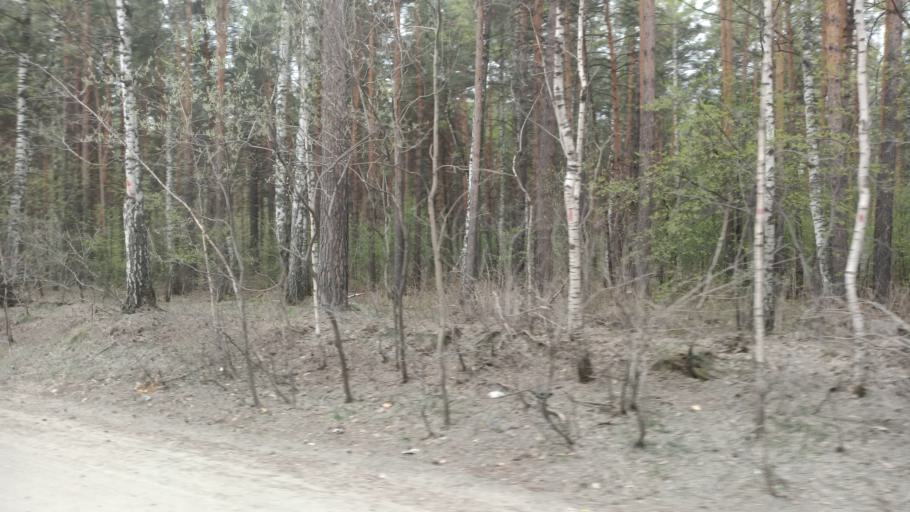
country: RU
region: Altai Krai
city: Yuzhnyy
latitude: 53.2791
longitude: 83.7180
